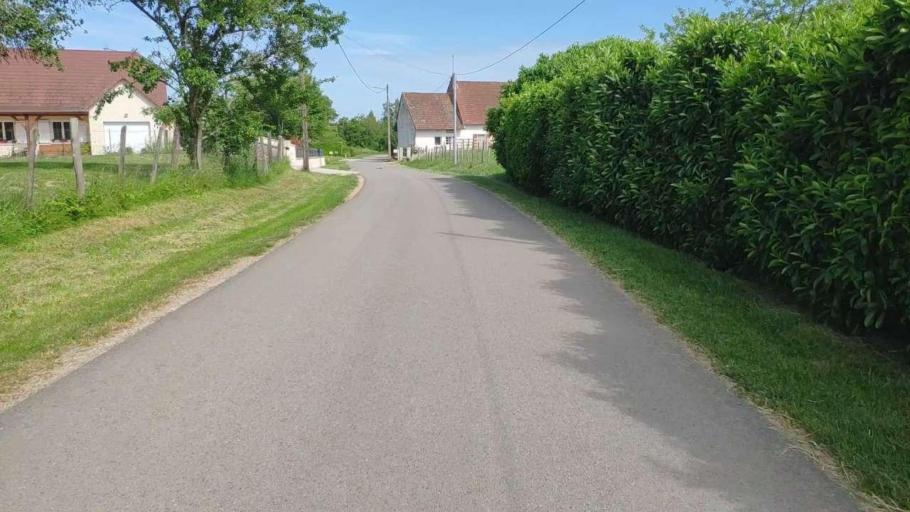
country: FR
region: Franche-Comte
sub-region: Departement du Jura
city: Bletterans
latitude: 46.7129
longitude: 5.4654
